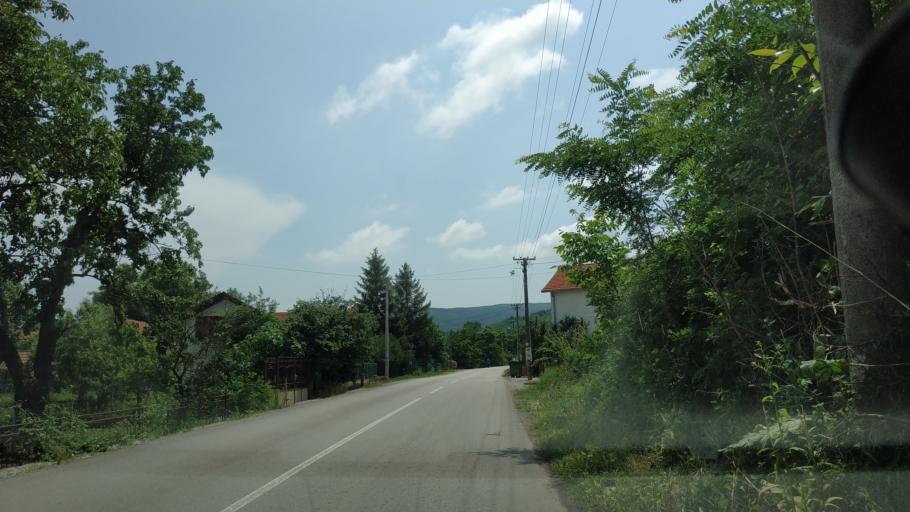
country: RS
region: Central Serbia
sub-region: Nisavski Okrug
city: Aleksinac
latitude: 43.4286
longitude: 21.7438
